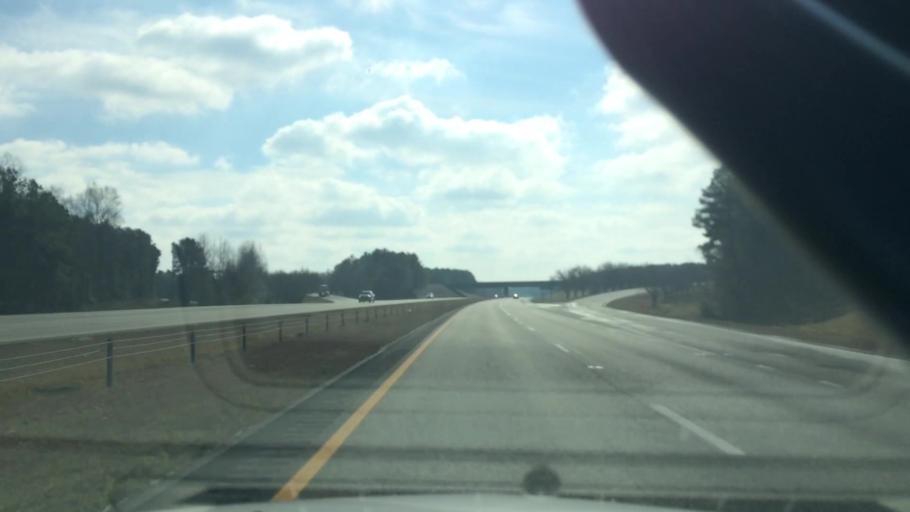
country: US
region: North Carolina
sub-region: Duplin County
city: Wallace
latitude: 34.6912
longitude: -77.9455
